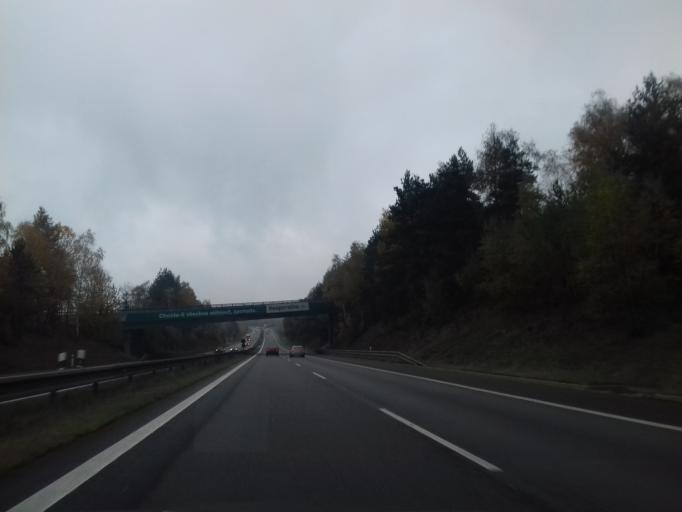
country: CZ
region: Vysocina
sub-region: Okres Pelhrimov
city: Zeliv
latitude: 49.5775
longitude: 15.2661
